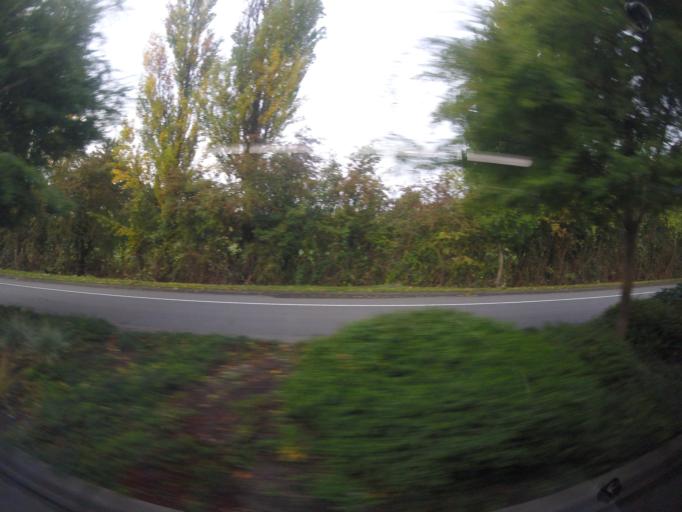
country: US
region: Washington
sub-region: King County
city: Medina
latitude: 47.6293
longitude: -122.2280
